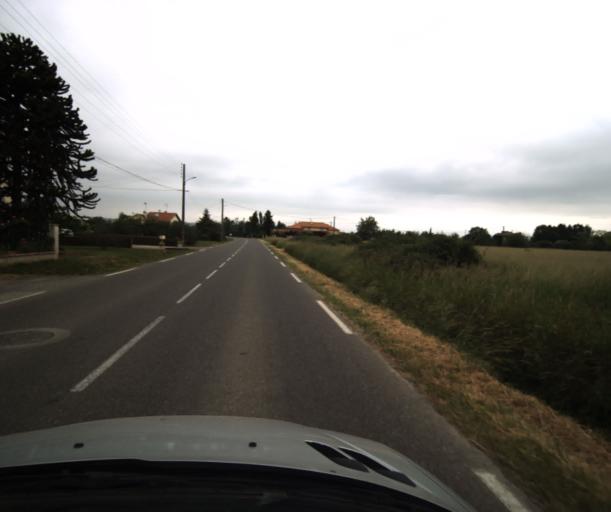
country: FR
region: Midi-Pyrenees
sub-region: Departement du Tarn-et-Garonne
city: Saint-Nicolas-de-la-Grave
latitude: 44.0547
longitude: 1.0258
